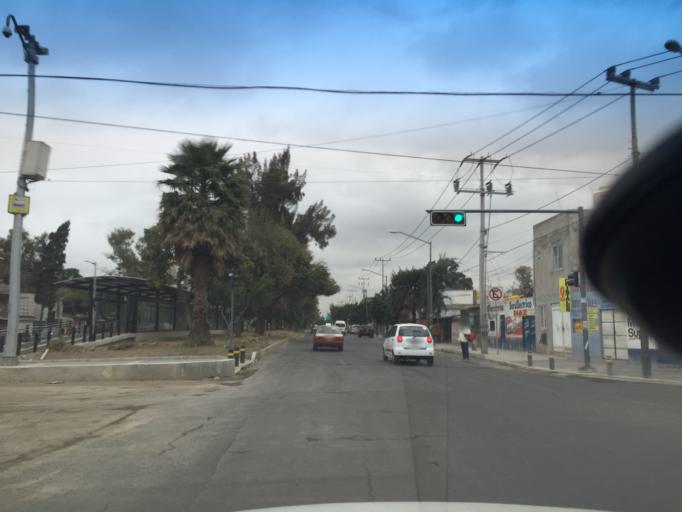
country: MX
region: Mexico City
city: Venustiano Carranza
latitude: 19.4717
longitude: -99.0709
